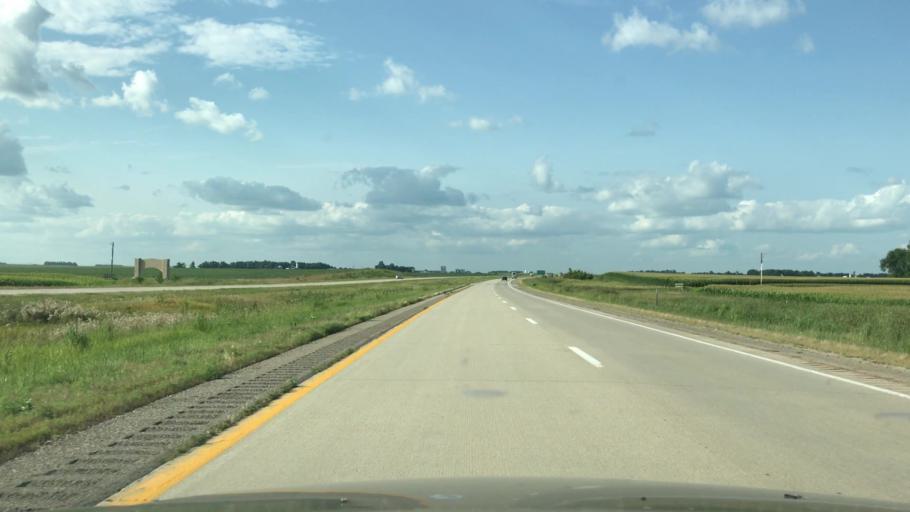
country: US
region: Iowa
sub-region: Osceola County
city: Sibley
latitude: 43.4170
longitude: -95.7168
